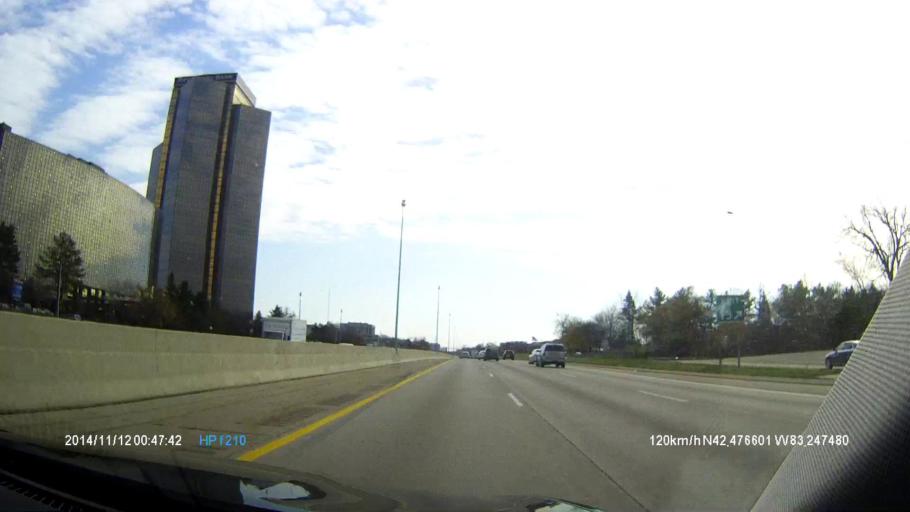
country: US
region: Michigan
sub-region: Oakland County
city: Southfield
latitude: 42.4765
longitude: -83.2473
